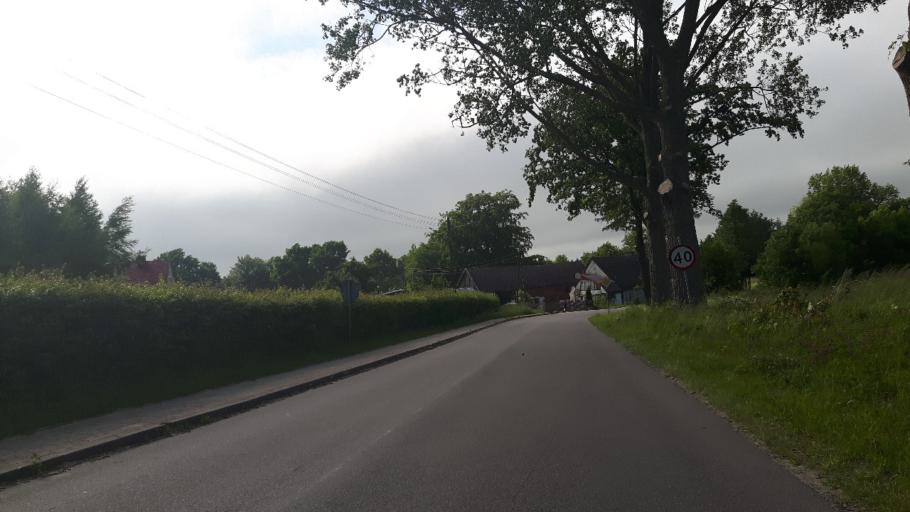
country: PL
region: Pomeranian Voivodeship
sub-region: Slupsk
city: Slupsk
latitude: 54.6143
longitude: 17.0339
